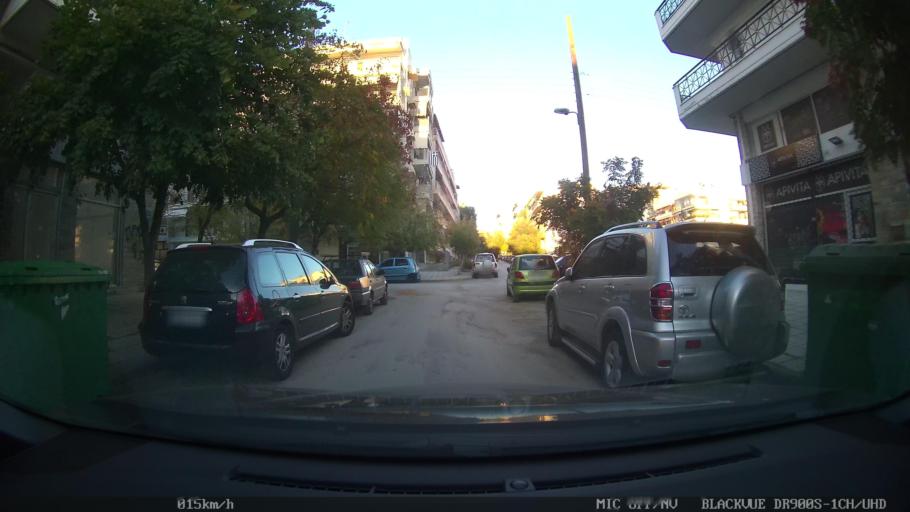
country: GR
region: Central Macedonia
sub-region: Nomos Thessalonikis
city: Pylaia
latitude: 40.6053
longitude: 22.9803
